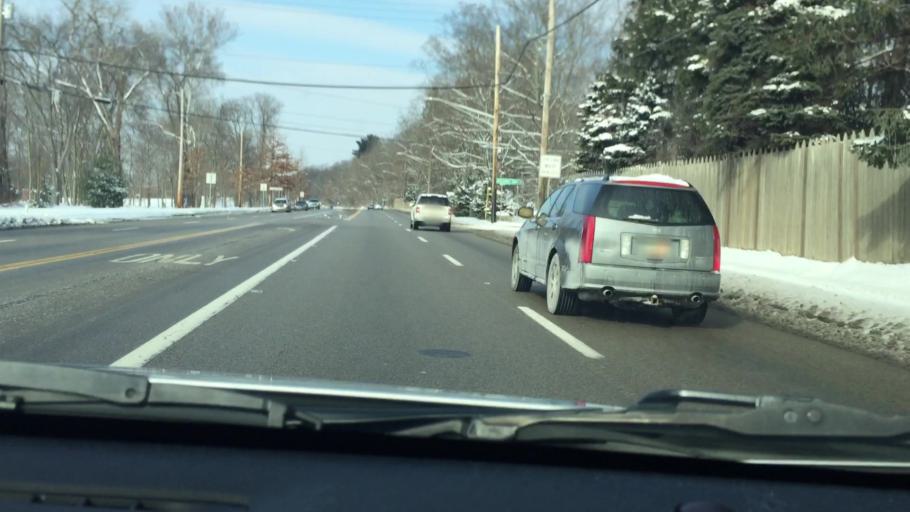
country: US
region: Pennsylvania
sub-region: Allegheny County
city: Edgeworth
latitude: 40.5468
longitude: -80.1949
